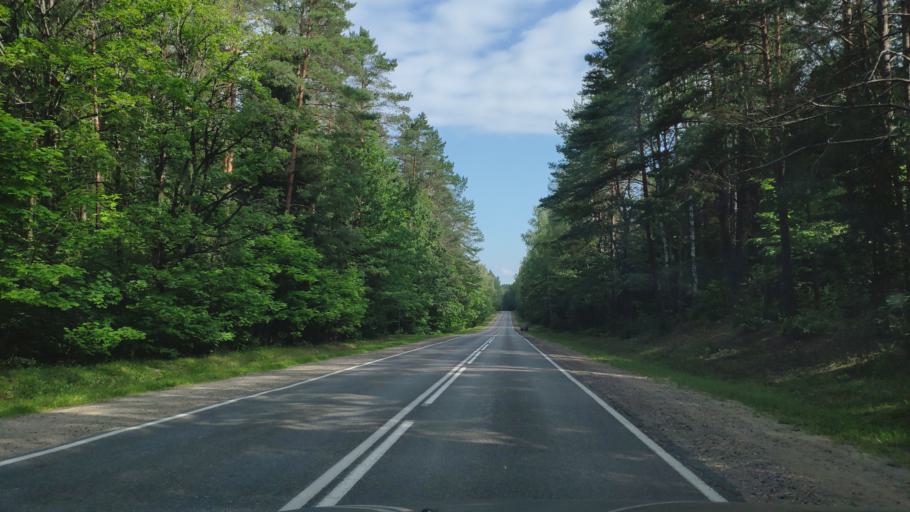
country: BY
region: Minsk
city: Novosel'ye
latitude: 53.9458
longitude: 27.2452
